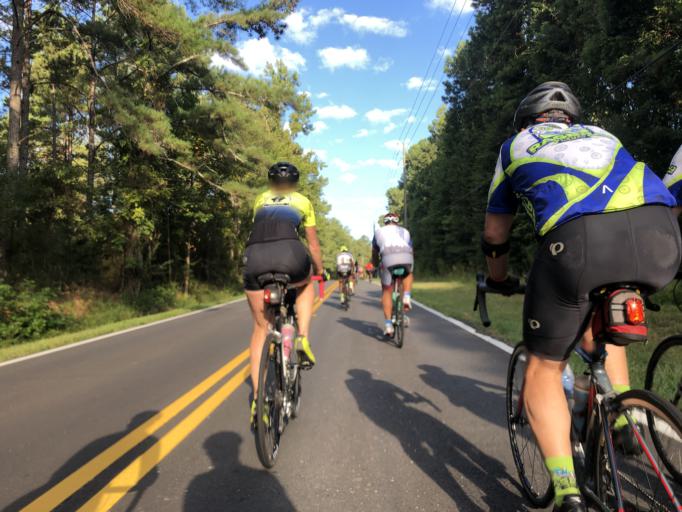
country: US
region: Georgia
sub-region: Fulton County
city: Palmetto
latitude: 33.5769
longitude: -84.6757
